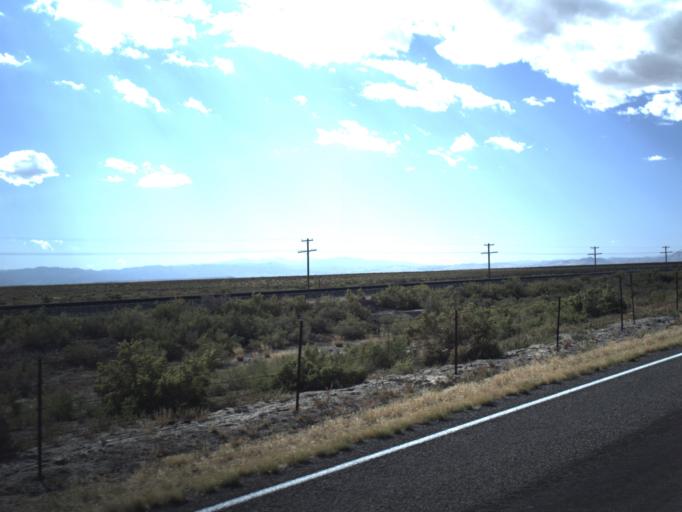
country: US
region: Utah
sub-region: Millard County
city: Delta
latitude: 39.0581
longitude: -112.7644
